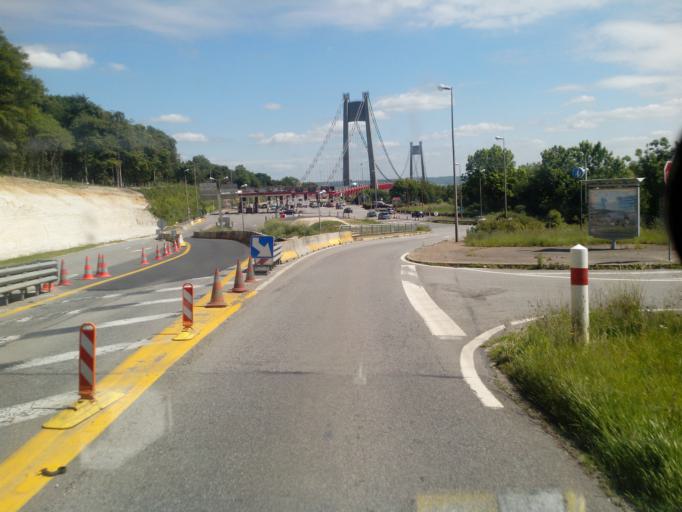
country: FR
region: Haute-Normandie
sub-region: Departement de la Seine-Maritime
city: Tancarville
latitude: 49.4784
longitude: 0.4574
